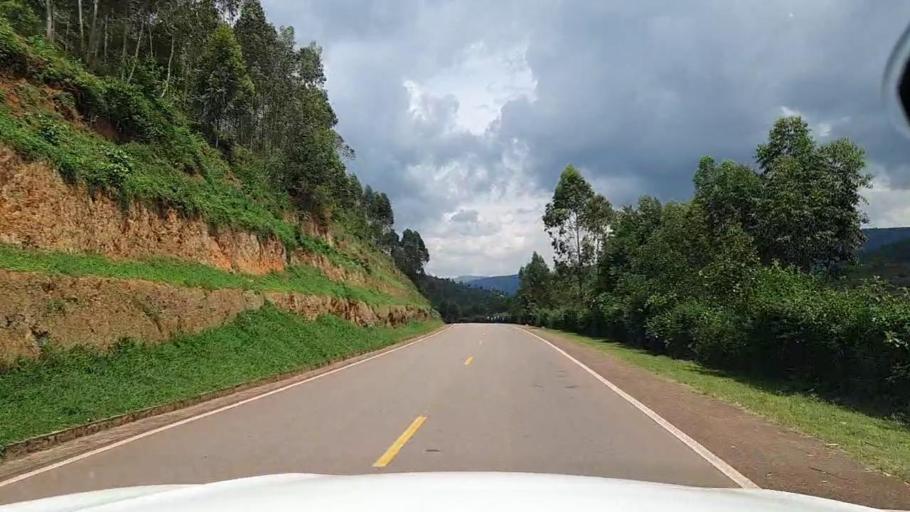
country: RW
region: Kigali
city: Kigali
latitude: -1.7980
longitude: 30.1290
